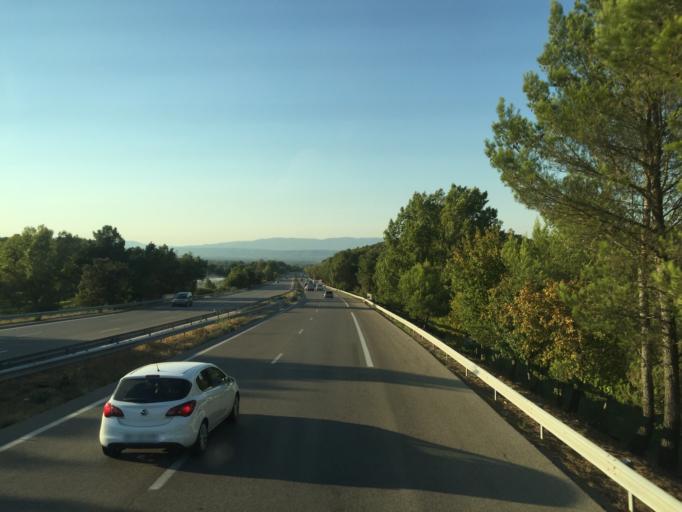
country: FR
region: Provence-Alpes-Cote d'Azur
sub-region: Departement des Bouches-du-Rhone
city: Venelles
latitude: 43.6131
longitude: 5.4974
